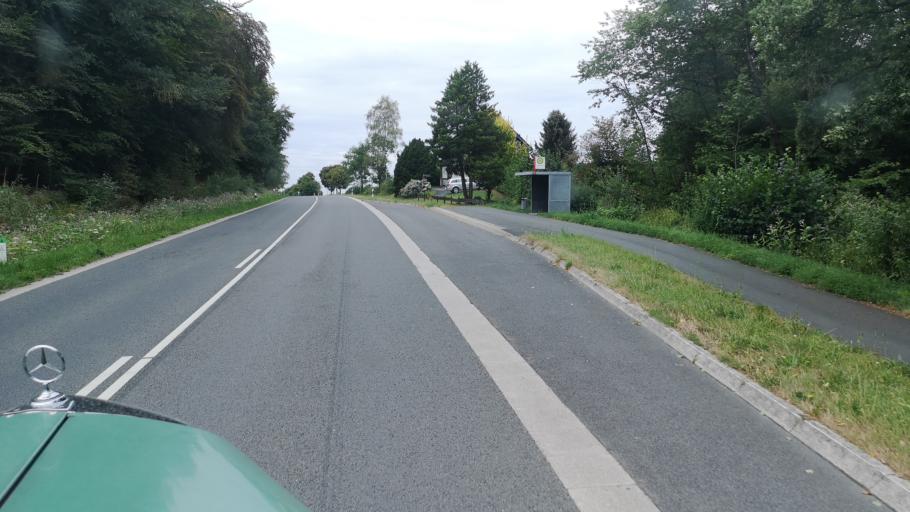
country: DE
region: North Rhine-Westphalia
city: Huckeswagen
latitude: 51.0999
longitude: 7.3366
